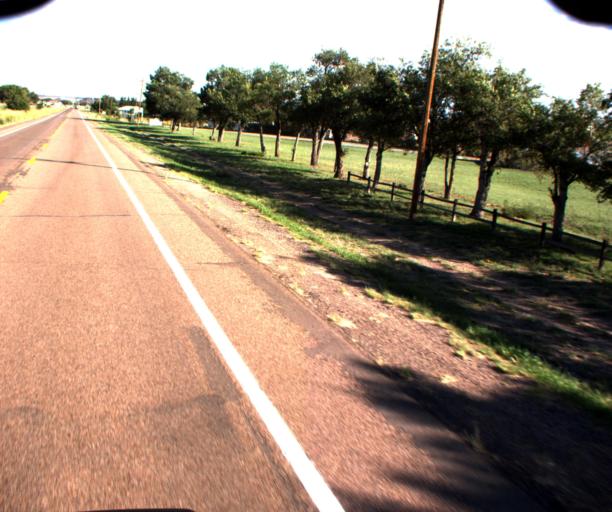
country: US
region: Arizona
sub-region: Apache County
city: Springerville
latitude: 34.1162
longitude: -109.2557
